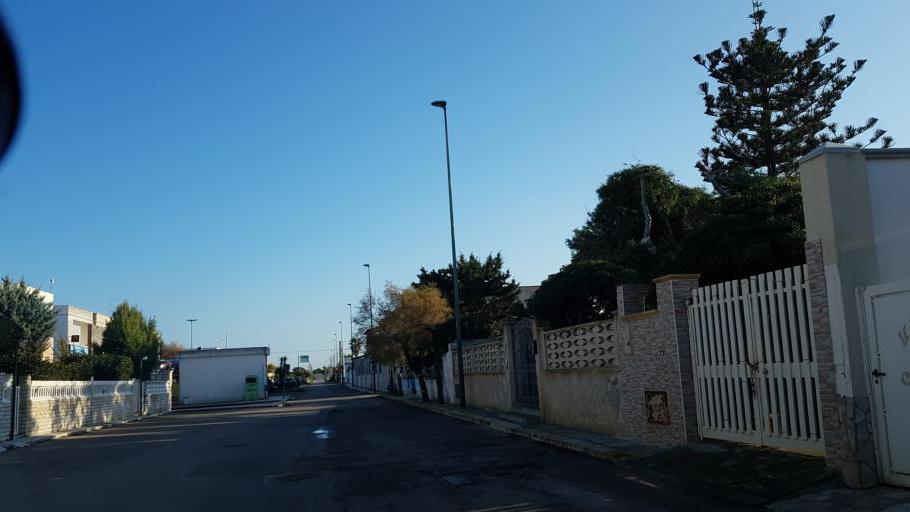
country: IT
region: Apulia
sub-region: Provincia di Brindisi
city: Torchiarolo
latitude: 40.5172
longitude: 18.0922
